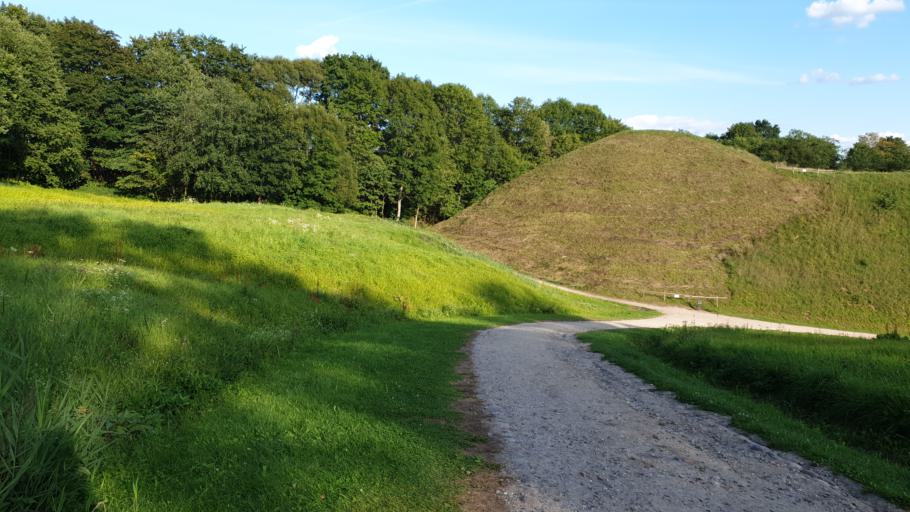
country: LT
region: Vilnius County
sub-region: Vilniaus Rajonas
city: Vievis
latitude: 54.8839
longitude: 24.8517
